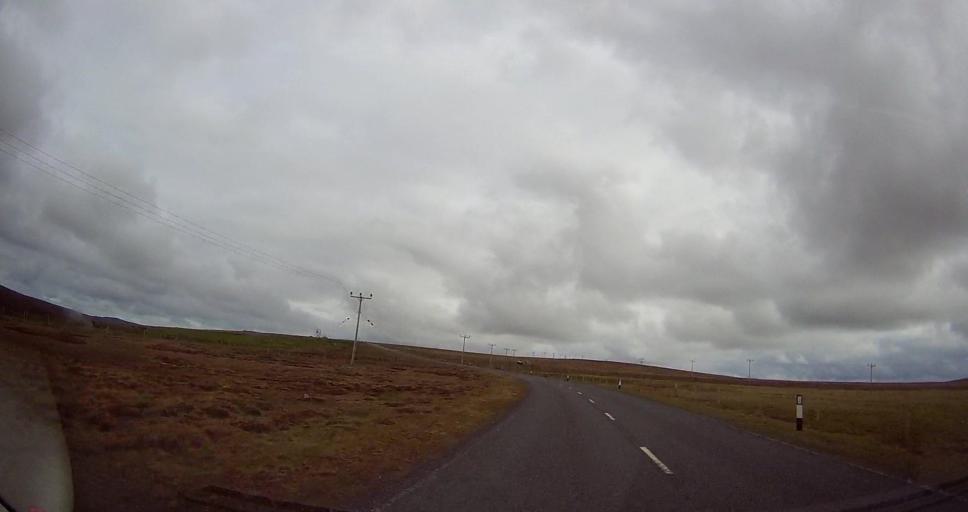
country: GB
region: Scotland
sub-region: Shetland Islands
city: Shetland
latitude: 60.7305
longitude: -0.8970
